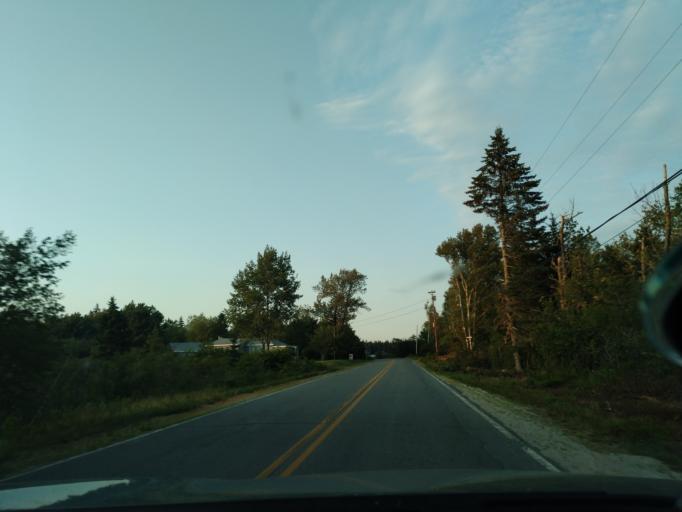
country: US
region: Maine
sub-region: Hancock County
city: Gouldsboro
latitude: 44.3697
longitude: -68.0354
